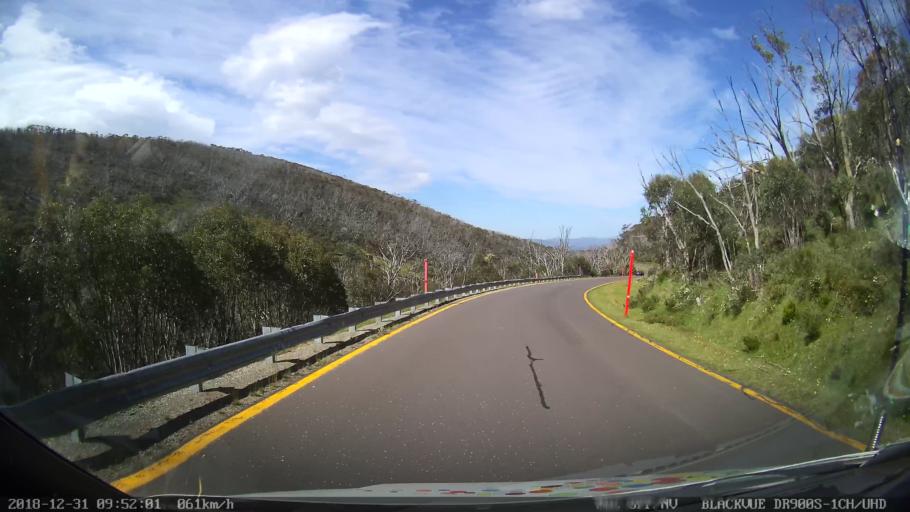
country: AU
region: New South Wales
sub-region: Snowy River
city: Jindabyne
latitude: -36.5250
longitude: 148.2573
